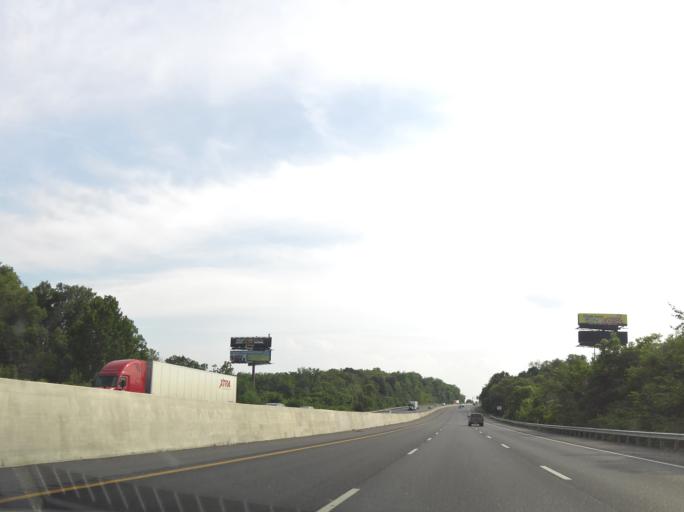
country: US
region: Maryland
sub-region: Washington County
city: Williamsport
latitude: 39.5713
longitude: -77.8868
